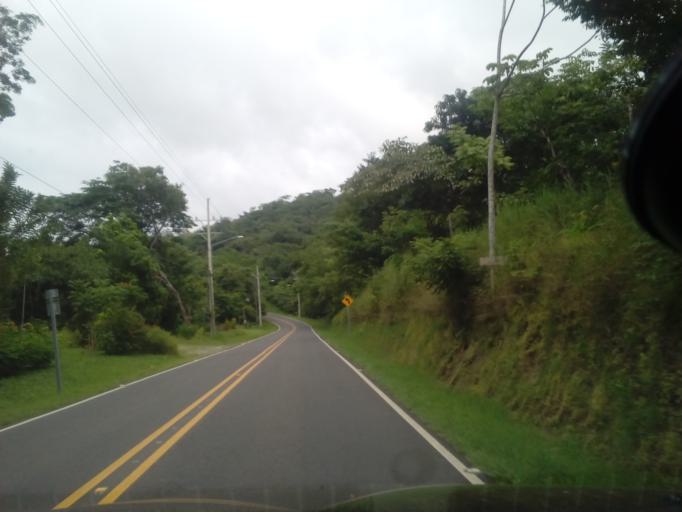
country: CR
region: Guanacaste
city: Samara
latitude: 9.9288
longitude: -85.5181
